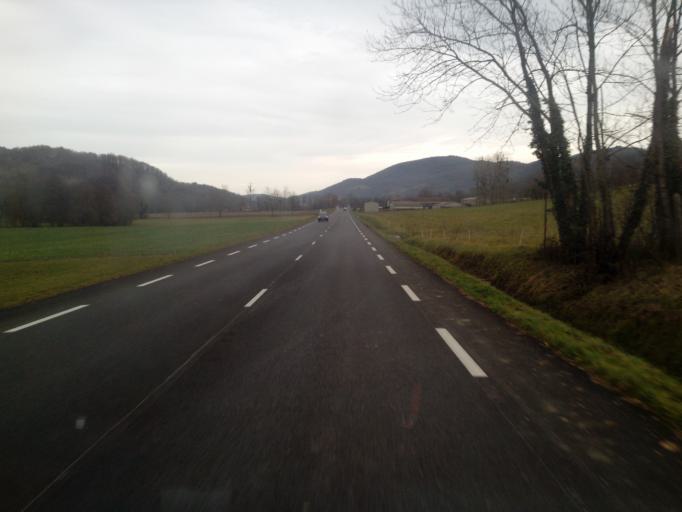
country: FR
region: Midi-Pyrenees
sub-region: Departement de l'Ariege
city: Foix
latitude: 43.0113
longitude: 1.4444
